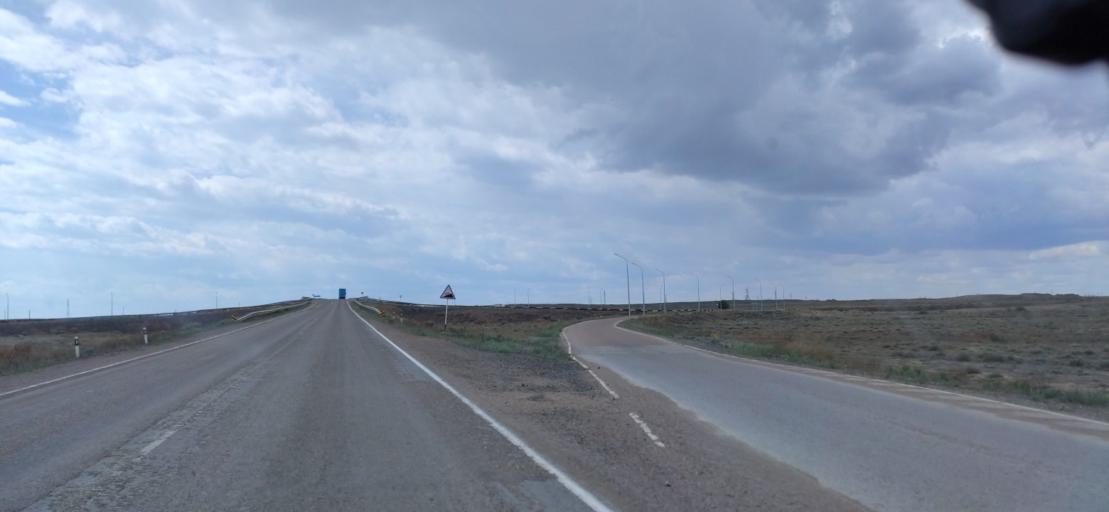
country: KZ
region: Qaraghandy
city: Saryshaghan
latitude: 46.0413
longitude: 73.5937
